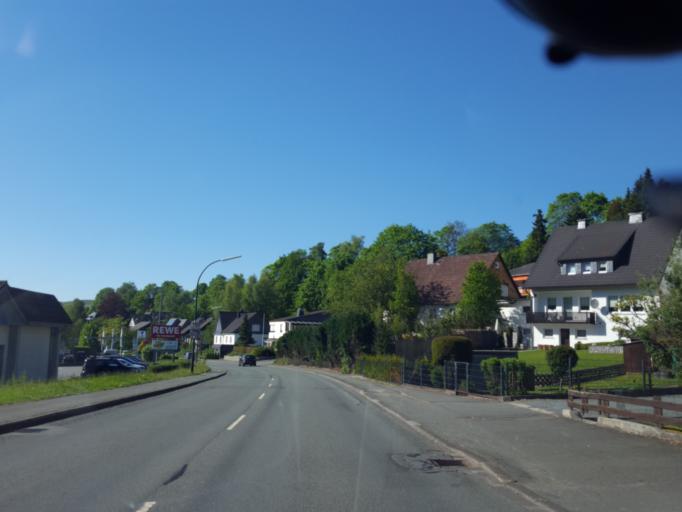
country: DE
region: North Rhine-Westphalia
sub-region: Regierungsbezirk Arnsberg
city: Winterberg
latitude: 51.2490
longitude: 8.4817
